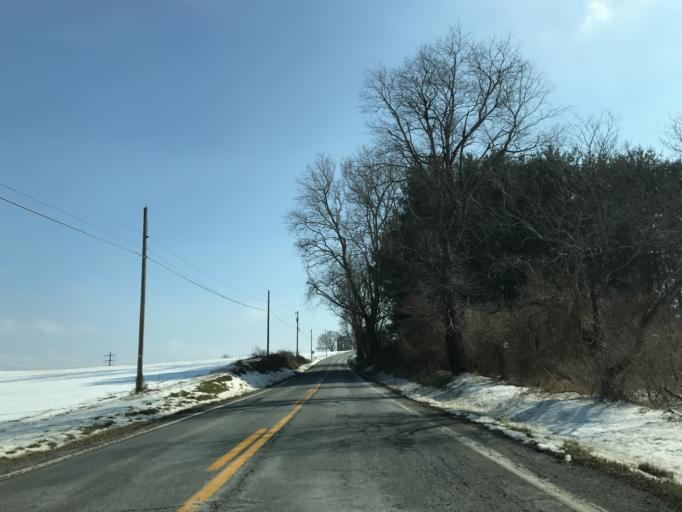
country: US
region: Pennsylvania
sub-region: York County
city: Susquehanna Trails
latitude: 39.6955
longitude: -76.3902
